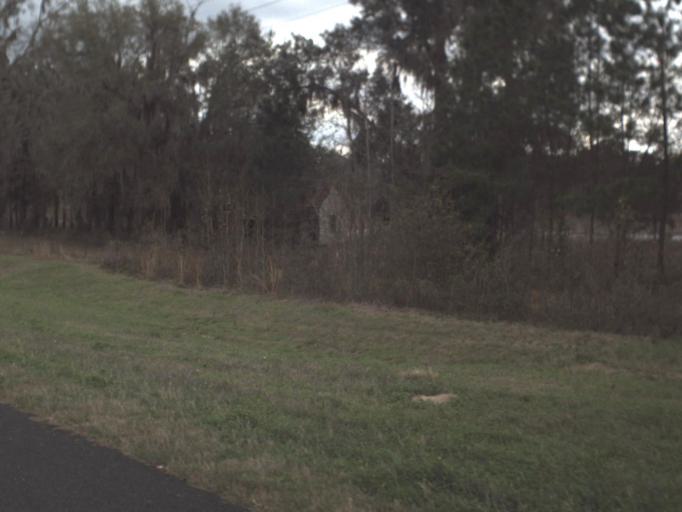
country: US
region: Florida
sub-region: Leon County
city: Tallahassee
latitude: 30.6109
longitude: -84.1754
